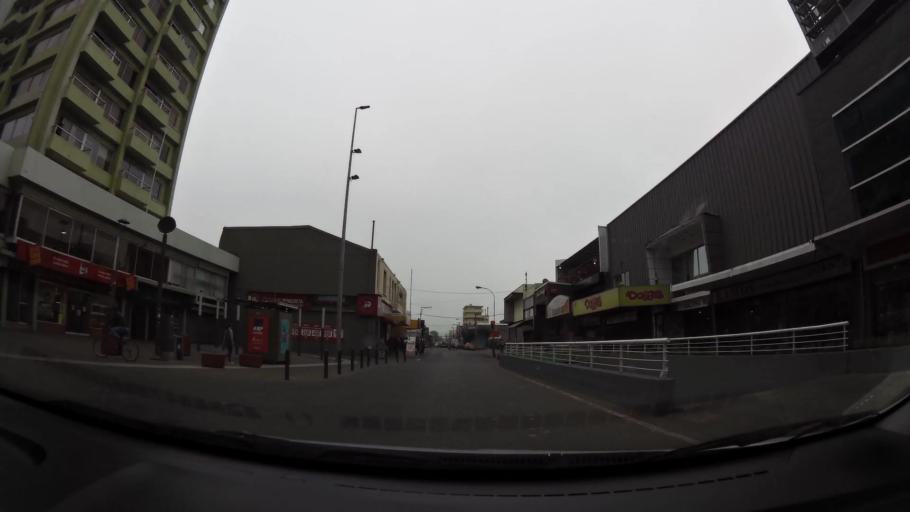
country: CL
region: Biobio
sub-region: Provincia de Concepcion
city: Concepcion
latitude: -36.8308
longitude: -73.0567
